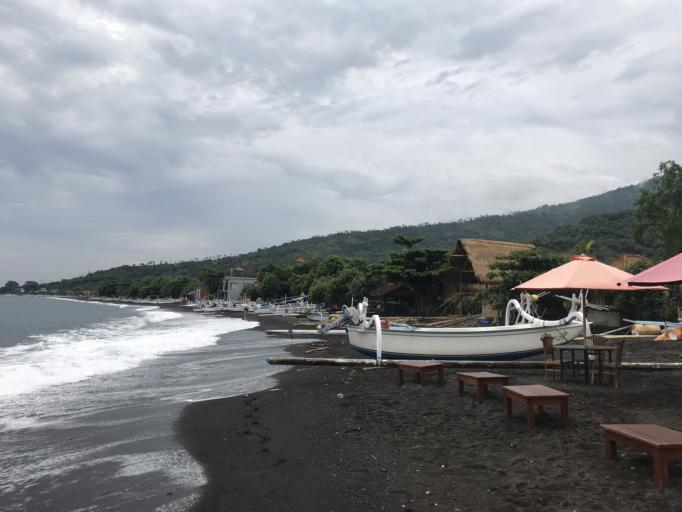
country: ID
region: Bali
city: Biaslantang Kaler
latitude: -8.3335
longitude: 115.6416
